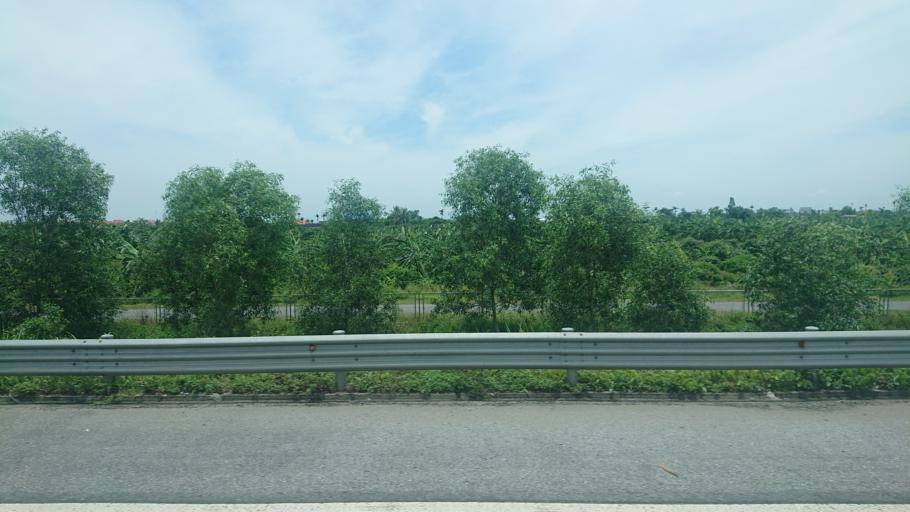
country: VN
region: Hai Duong
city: Tu Ky
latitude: 20.8266
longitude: 106.4604
